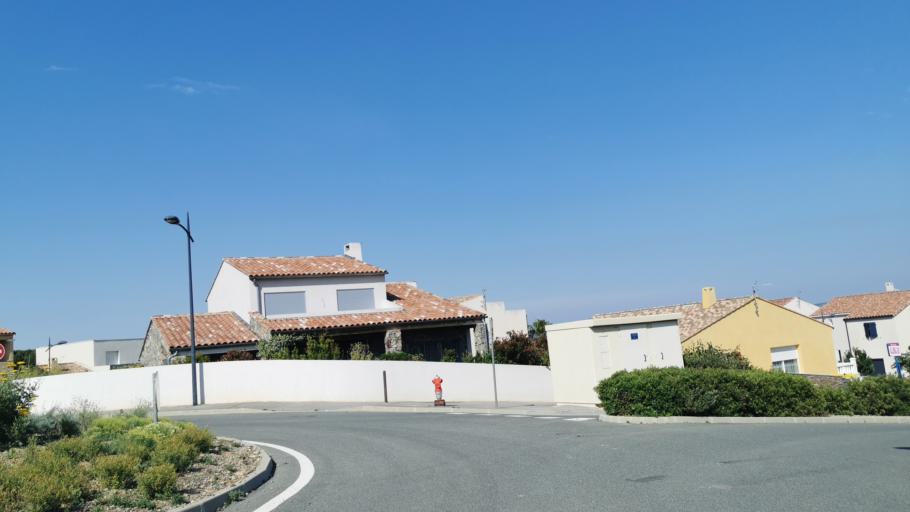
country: FR
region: Languedoc-Roussillon
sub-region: Departement de l'Aude
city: Peyriac-de-Mer
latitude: 43.1370
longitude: 2.9624
